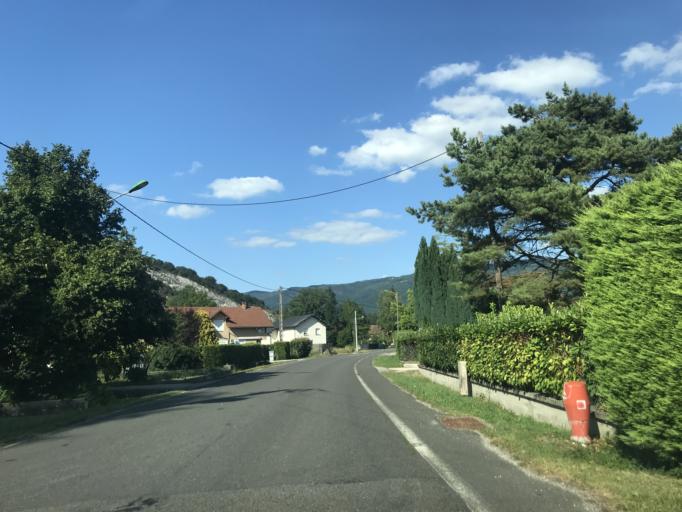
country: FR
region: Rhone-Alpes
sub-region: Departement de l'Ain
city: Culoz
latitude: 45.8218
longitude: 5.8031
